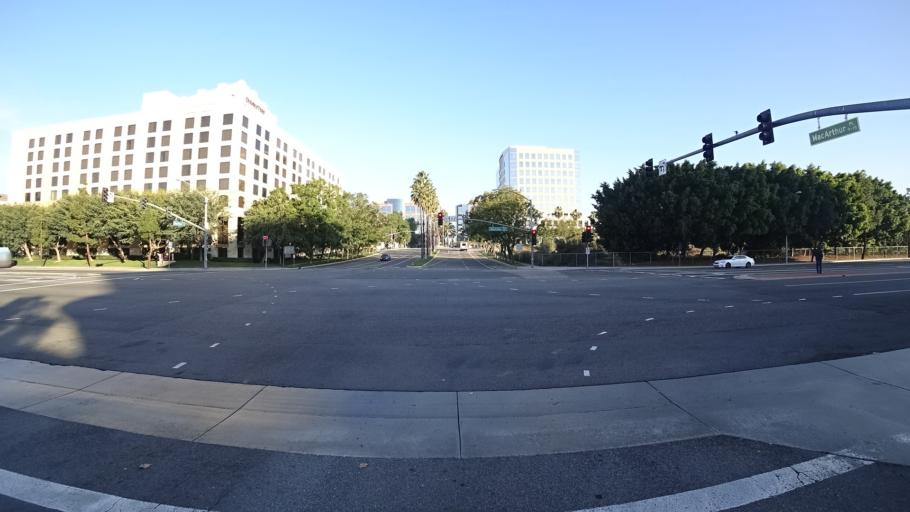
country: US
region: California
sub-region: Orange County
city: Santa Ana
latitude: 33.6998
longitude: -117.8656
